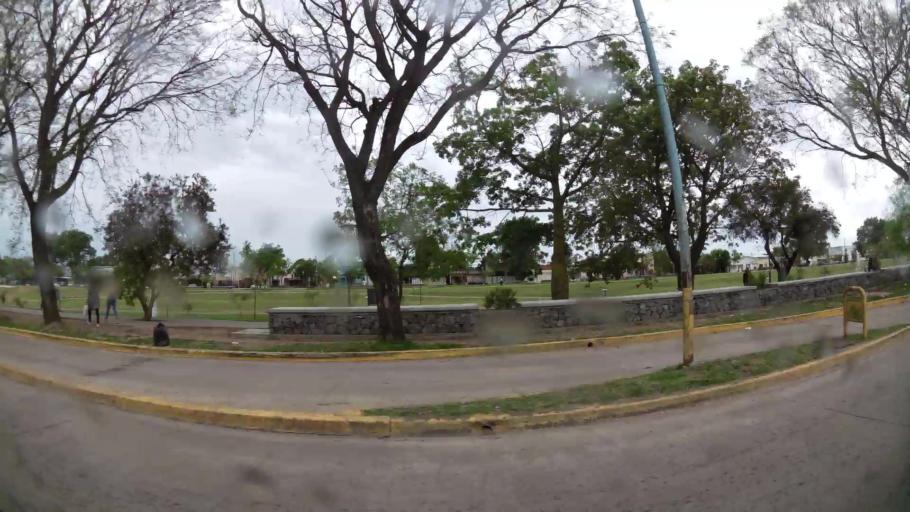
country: AR
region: Buenos Aires
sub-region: Partido de Zarate
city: Zarate
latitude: -34.1057
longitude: -59.0255
